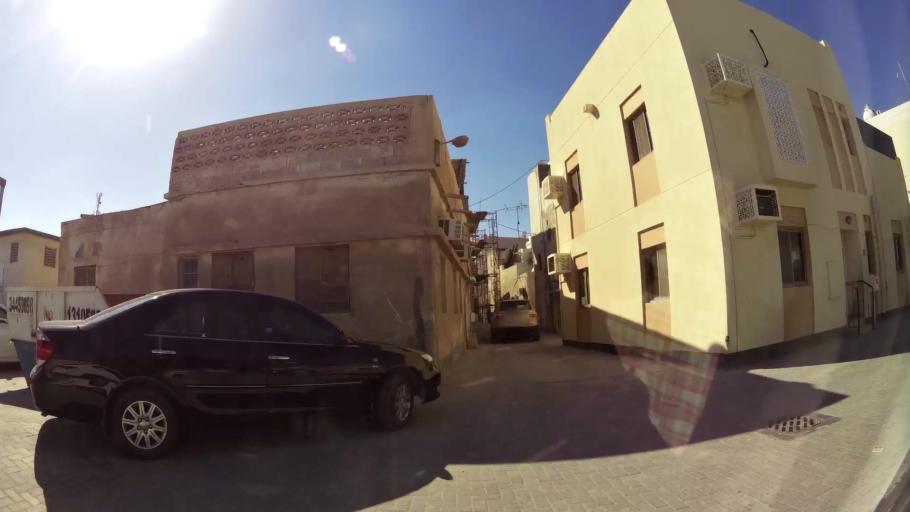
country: BH
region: Muharraq
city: Al Hadd
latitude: 26.2372
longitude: 50.6540
